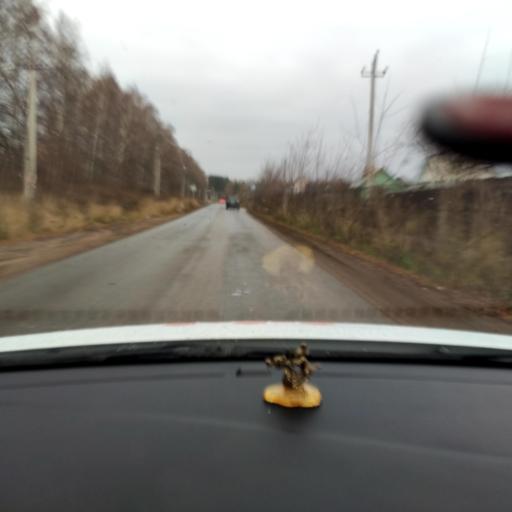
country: RU
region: Tatarstan
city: Vysokaya Gora
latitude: 55.8261
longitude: 49.2410
